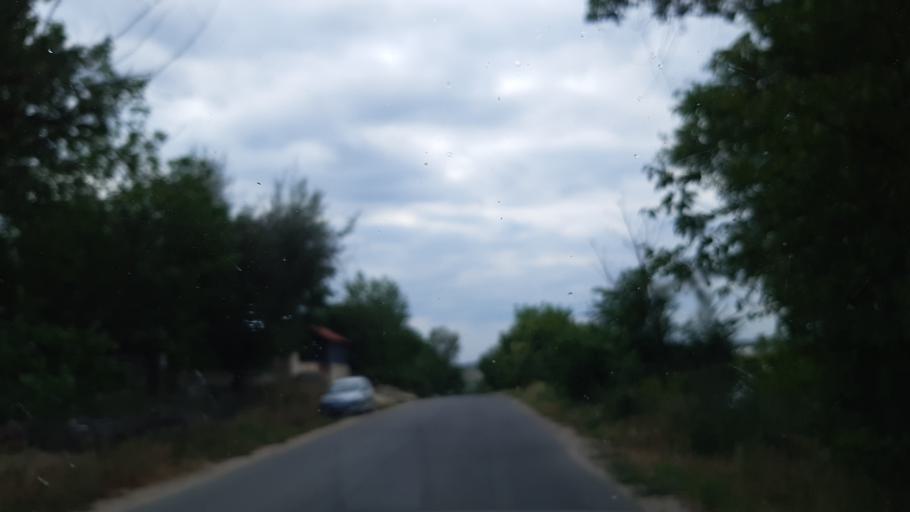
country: MD
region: Chisinau
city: Vatra
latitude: 47.0540
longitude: 28.7313
